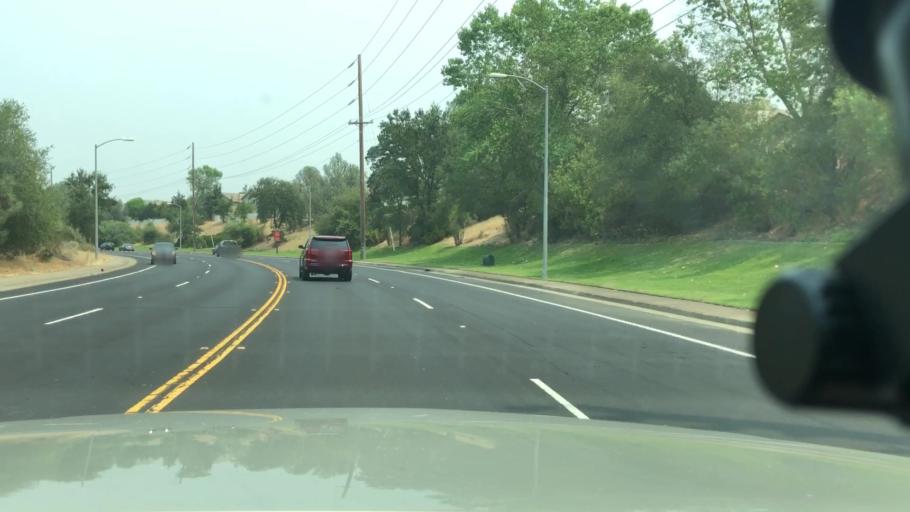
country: US
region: California
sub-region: Sacramento County
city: Folsom
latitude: 38.6582
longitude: -121.1602
